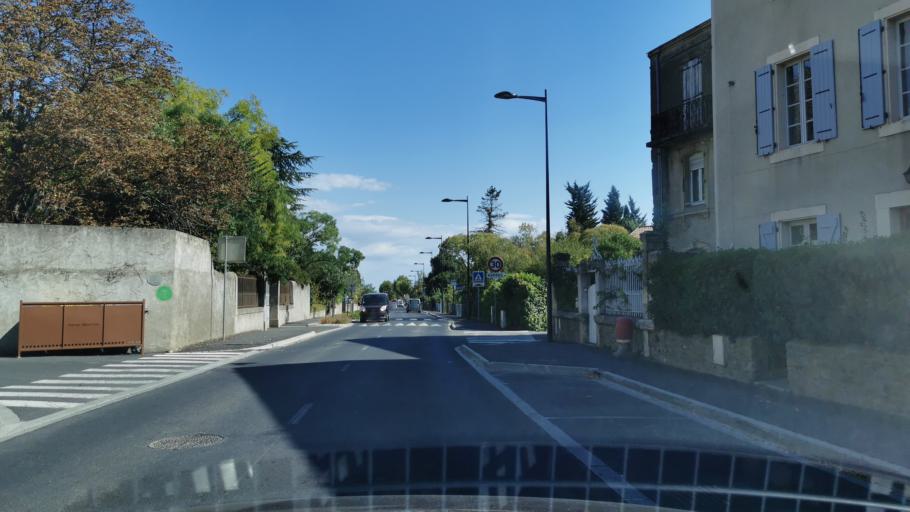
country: FR
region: Languedoc-Roussillon
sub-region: Departement de l'Aude
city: Peyriac-Minervois
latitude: 43.2895
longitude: 2.5671
